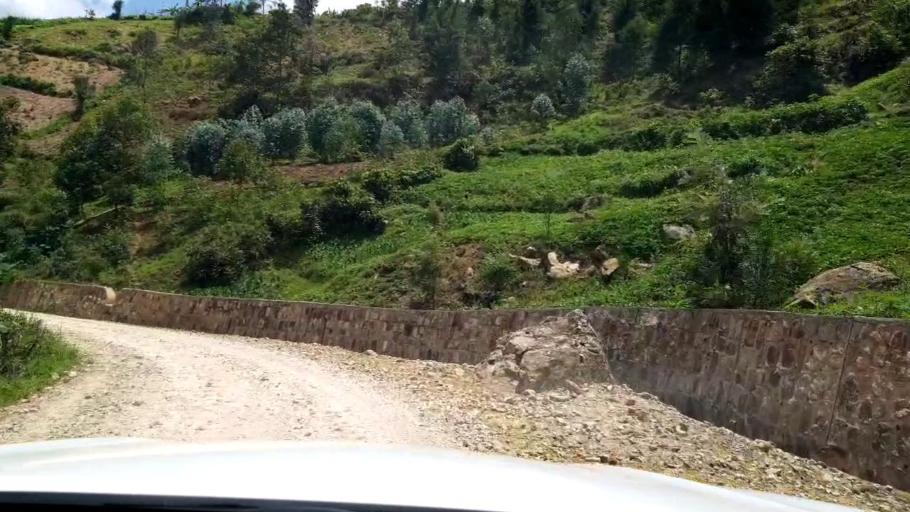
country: RW
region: Southern Province
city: Gitarama
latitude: -1.9838
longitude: 29.6204
